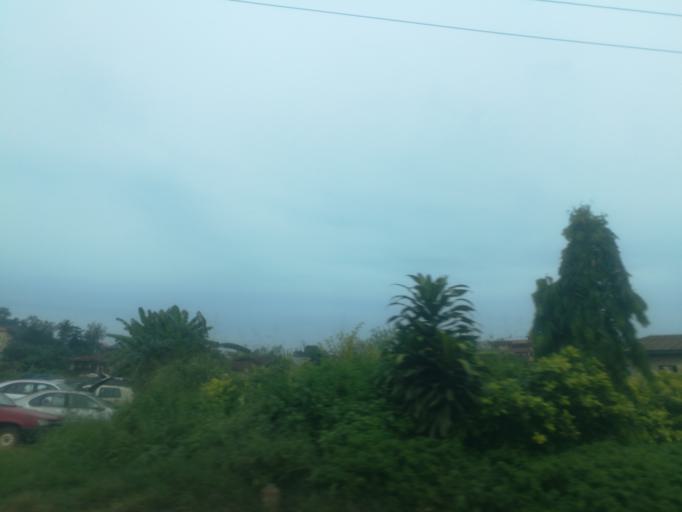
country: NG
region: Oyo
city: Egbeda
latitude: 7.3827
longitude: 3.9925
